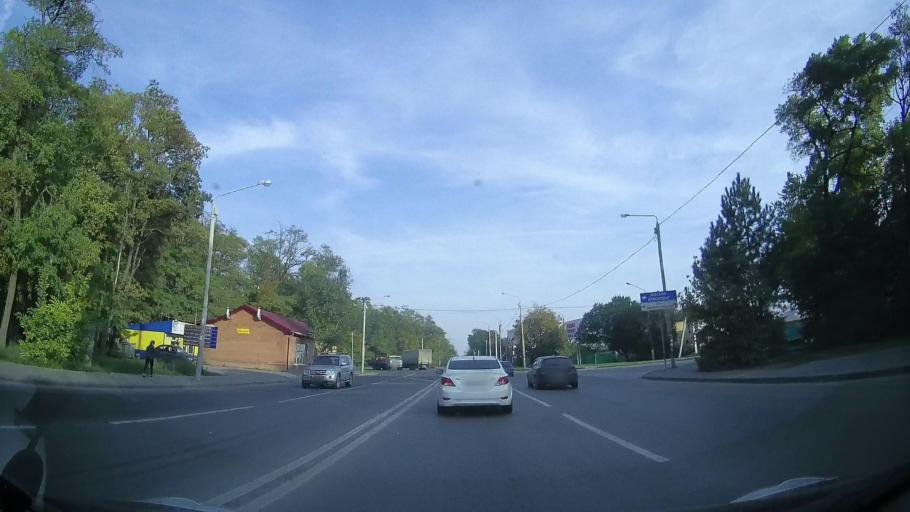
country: RU
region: Rostov
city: Imeni Chkalova
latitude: 47.2747
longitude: 39.7934
